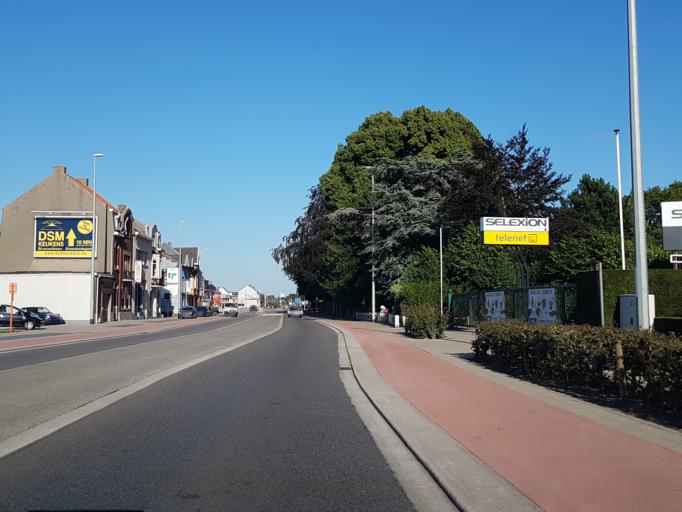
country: BE
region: Flanders
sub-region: Provincie Oost-Vlaanderen
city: Aalst
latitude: 50.9408
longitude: 4.0070
